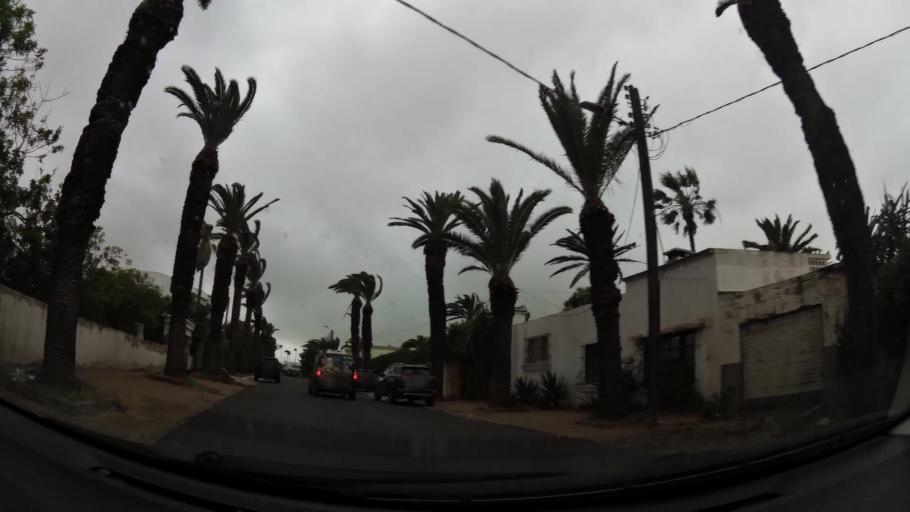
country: MA
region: Grand Casablanca
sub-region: Casablanca
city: Casablanca
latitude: 33.5902
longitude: -7.6777
